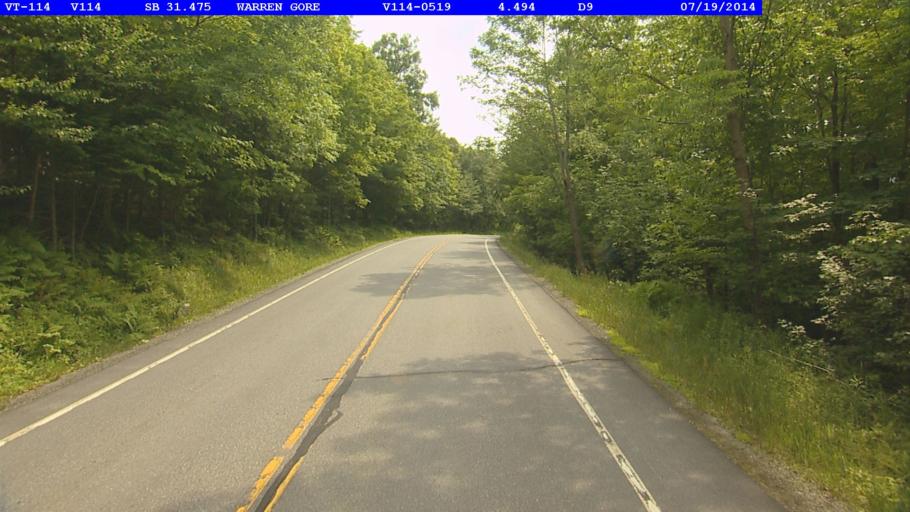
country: CA
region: Quebec
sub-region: Estrie
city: Coaticook
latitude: 44.9422
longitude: -71.8509
